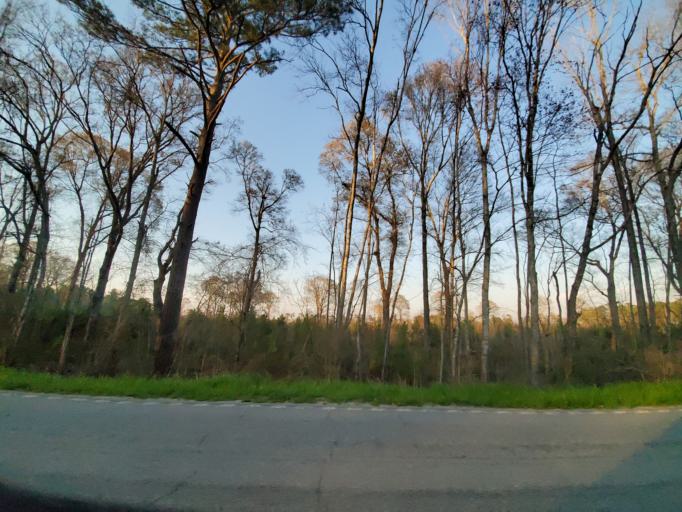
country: US
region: South Carolina
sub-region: Dorchester County
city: Ridgeville
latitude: 33.0474
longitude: -80.4546
